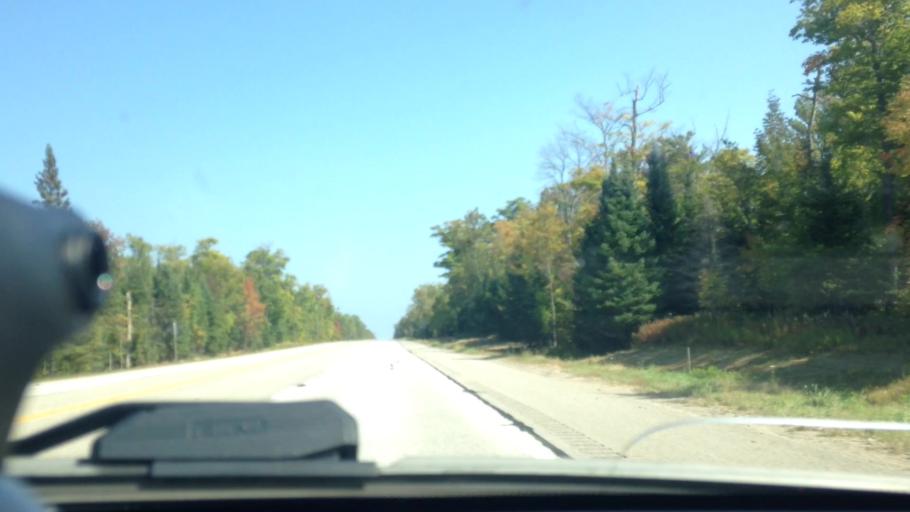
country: US
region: Michigan
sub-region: Luce County
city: Newberry
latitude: 46.3036
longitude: -85.2889
